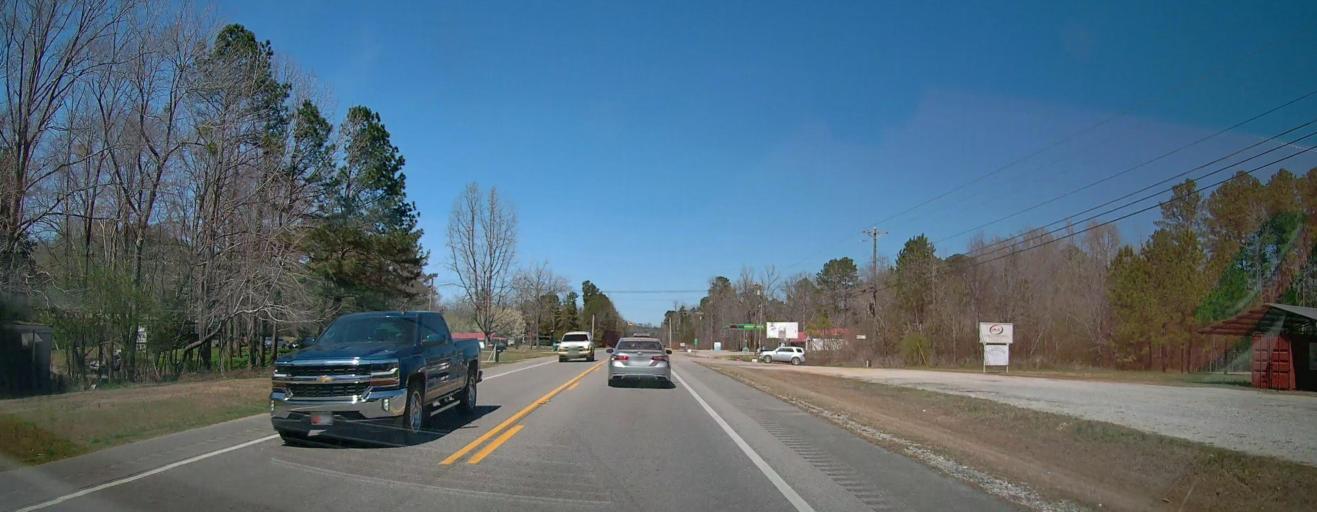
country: US
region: Alabama
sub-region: Calhoun County
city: Ohatchee
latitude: 33.8208
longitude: -86.0401
